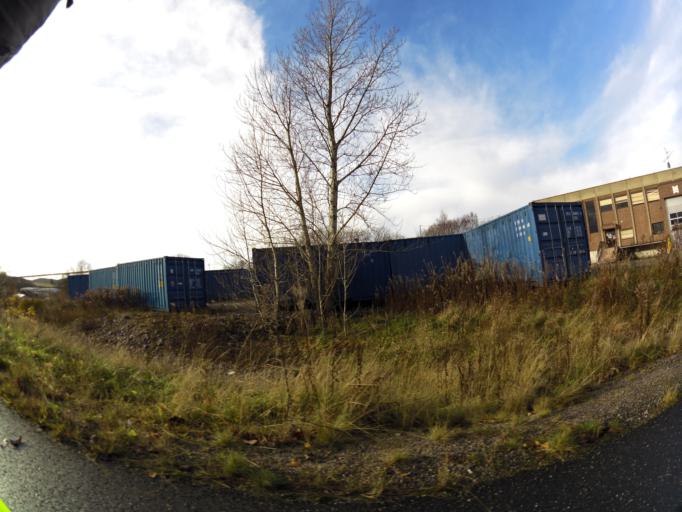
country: NO
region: Ostfold
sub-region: Sarpsborg
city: Sarpsborg
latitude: 59.2710
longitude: 11.0804
